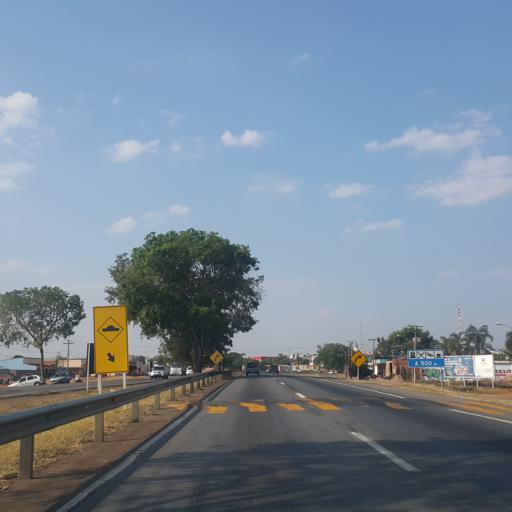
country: BR
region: Goias
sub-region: Abadiania
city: Abadiania
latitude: -16.0918
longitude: -48.5142
